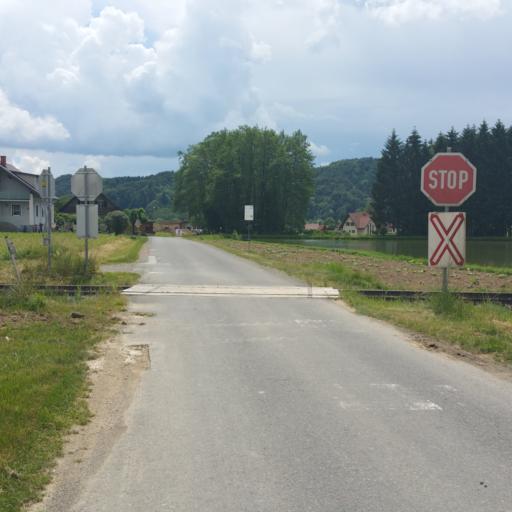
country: AT
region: Styria
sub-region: Politischer Bezirk Leibnitz
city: Gleinstatten
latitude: 46.7470
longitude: 15.3421
